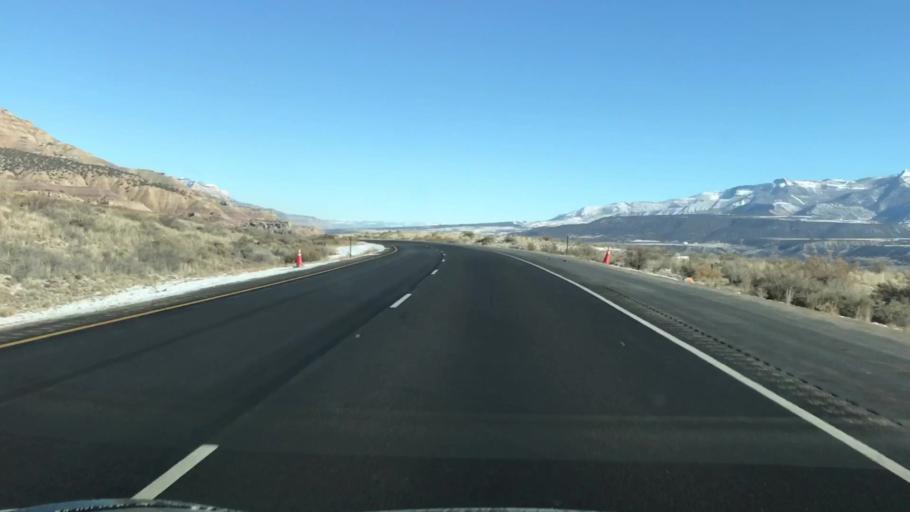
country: US
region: Colorado
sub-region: Garfield County
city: Parachute
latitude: 39.3903
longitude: -108.1314
